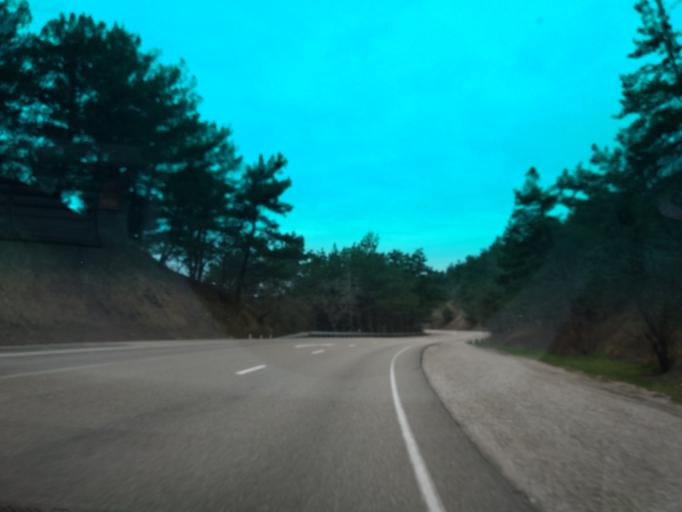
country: RU
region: Krasnodarskiy
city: Ol'ginka
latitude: 44.1862
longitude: 38.9133
